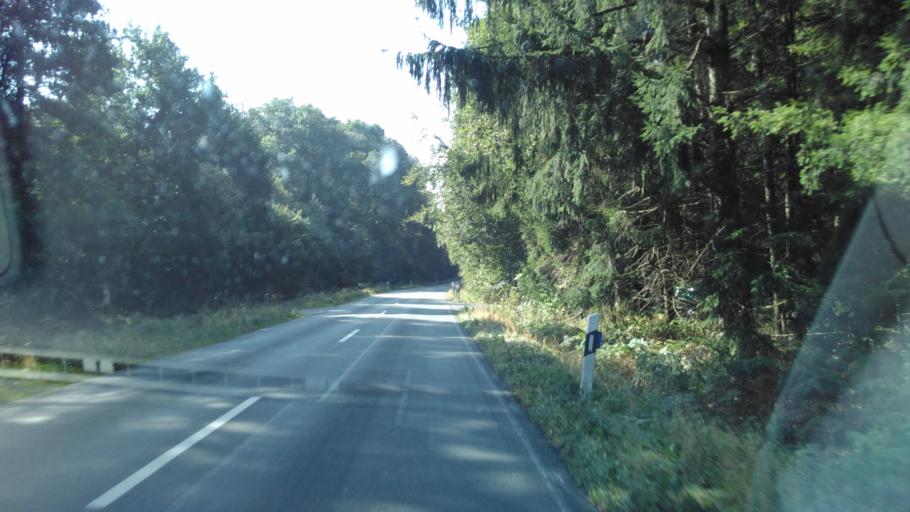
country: DE
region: North Rhine-Westphalia
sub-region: Regierungsbezirk Detmold
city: Verl
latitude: 51.8925
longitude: 8.5930
